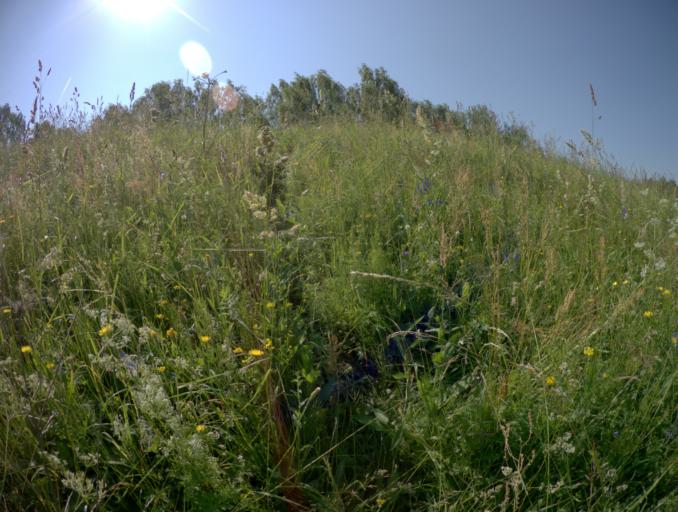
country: RU
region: Vladimir
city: Novovyazniki
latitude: 56.2350
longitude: 42.2445
